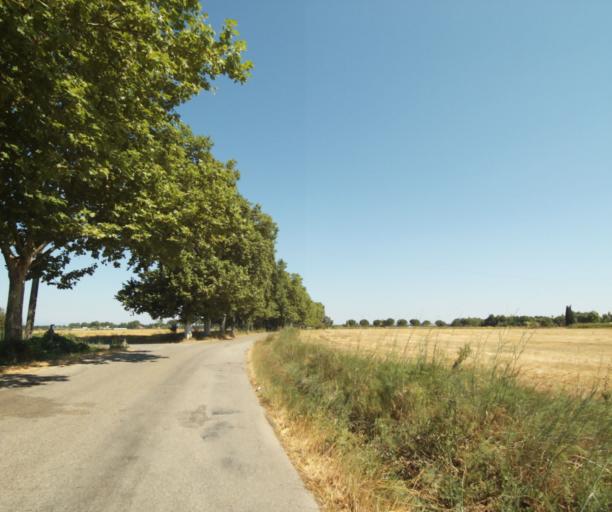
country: FR
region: Languedoc-Roussillon
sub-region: Departement de l'Herault
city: Marsillargues
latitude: 43.6630
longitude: 4.1601
